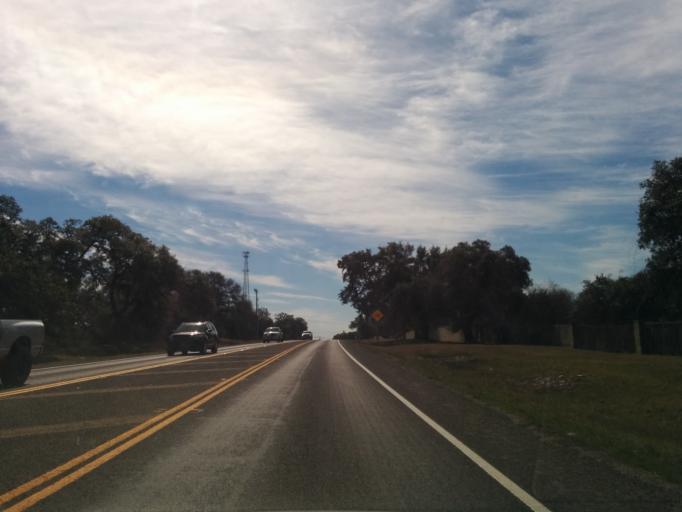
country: US
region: Texas
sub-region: Bexar County
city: Fair Oaks Ranch
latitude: 29.7374
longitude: -98.6234
